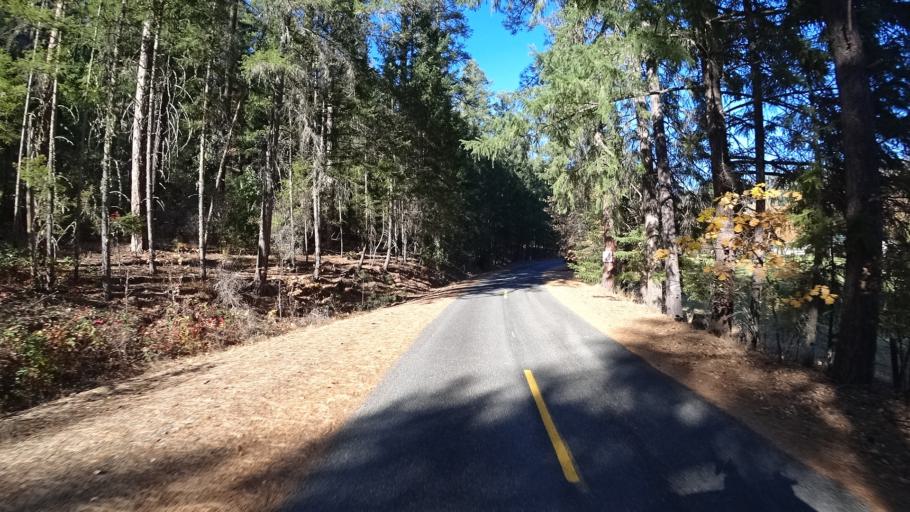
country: US
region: California
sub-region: Siskiyou County
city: Yreka
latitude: 41.8220
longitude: -122.9744
